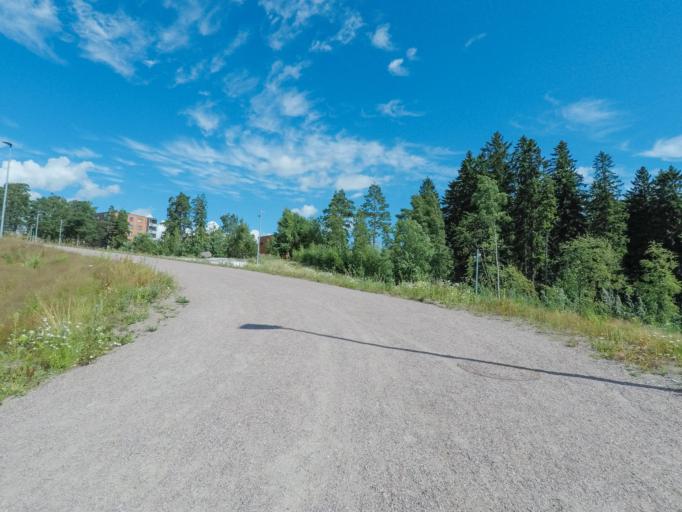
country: FI
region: Uusimaa
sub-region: Helsinki
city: Vantaa
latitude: 60.2180
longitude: 25.0735
